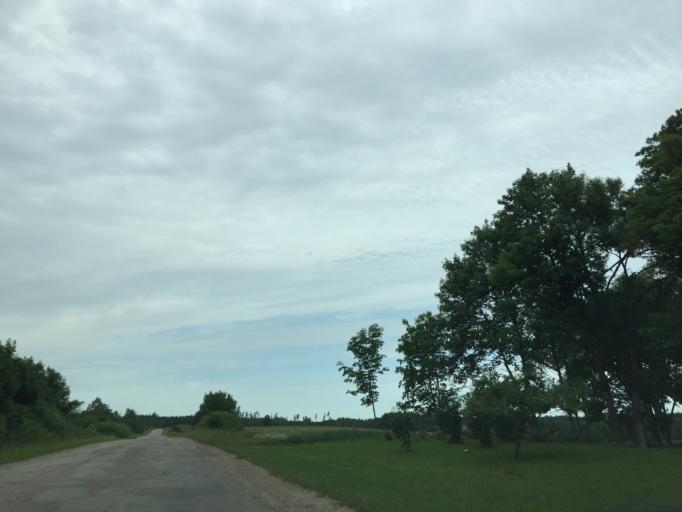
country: LV
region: Tukuma Rajons
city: Tukums
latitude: 57.0448
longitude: 23.1228
